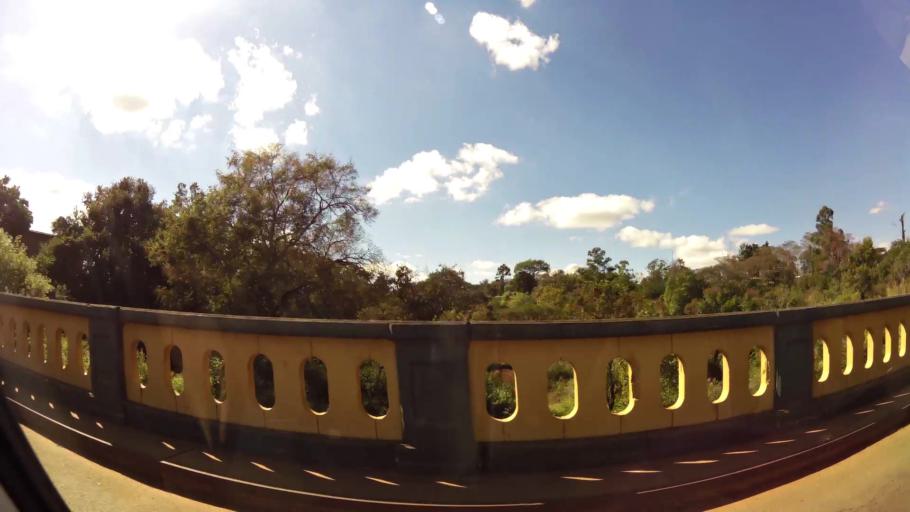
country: ZA
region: Limpopo
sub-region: Mopani District Municipality
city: Tzaneen
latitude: -23.8212
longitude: 30.1661
